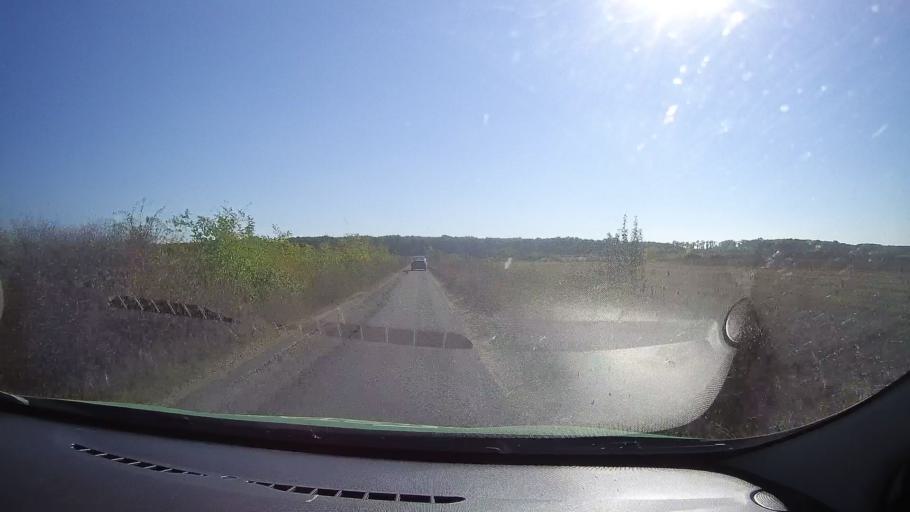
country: RO
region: Satu Mare
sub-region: Comuna Doba
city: Doba
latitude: 47.7218
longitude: 22.7256
